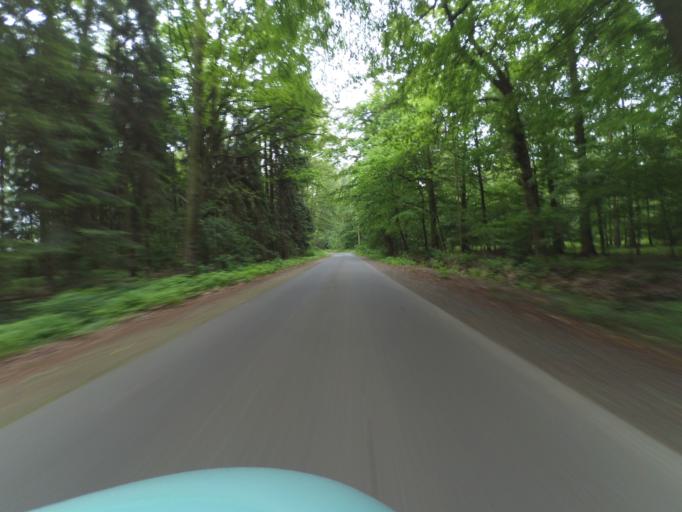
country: DE
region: Lower Saxony
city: Uetze
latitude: 52.4921
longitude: 10.1679
